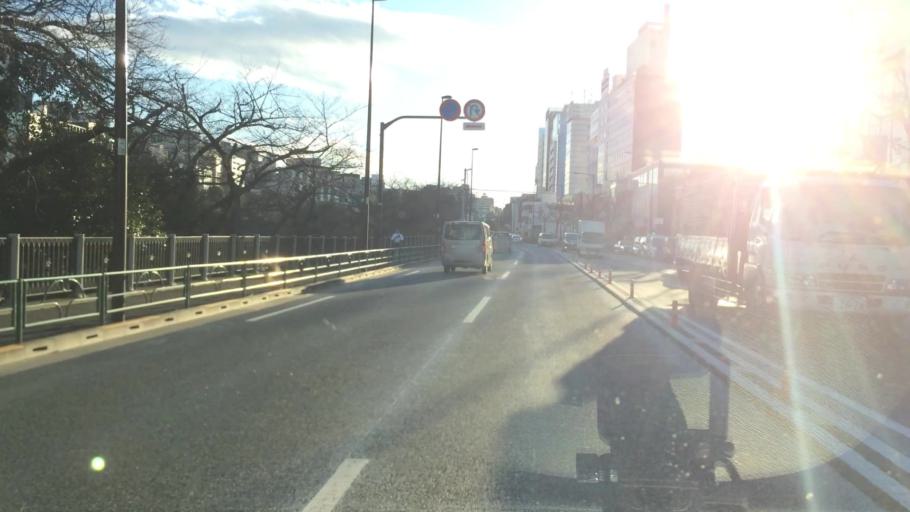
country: JP
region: Tokyo
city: Tokyo
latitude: 35.6974
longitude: 139.7401
